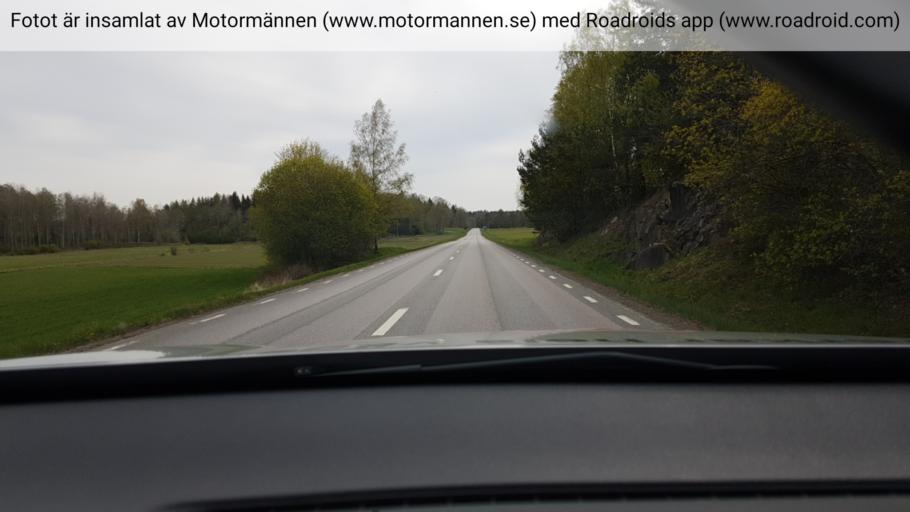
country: SE
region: Stockholm
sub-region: Norrtalje Kommun
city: Nykvarn
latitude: 59.9255
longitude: 18.1087
